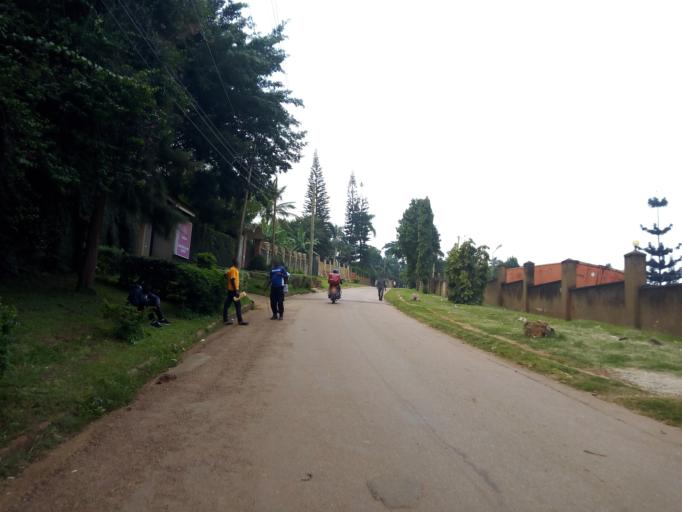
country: UG
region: Central Region
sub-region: Wakiso District
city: Kireka
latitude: 0.3202
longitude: 32.6263
